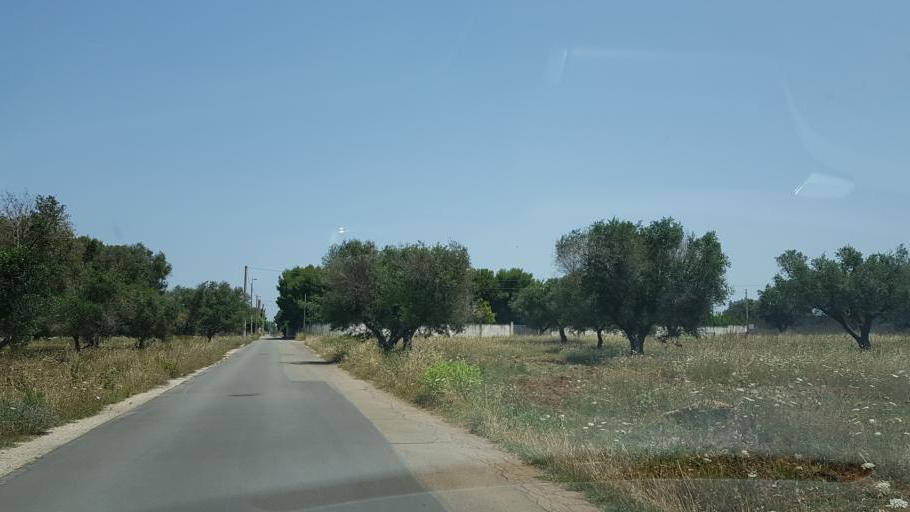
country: IT
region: Apulia
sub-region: Provincia di Lecce
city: Porto Cesareo
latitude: 40.2531
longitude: 17.9163
